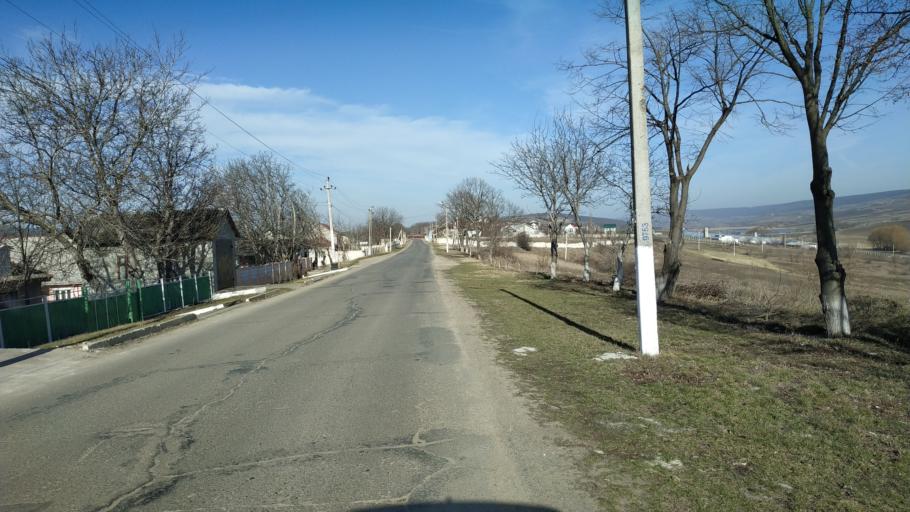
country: MD
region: Chisinau
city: Vatra
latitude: 47.0174
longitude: 28.6530
